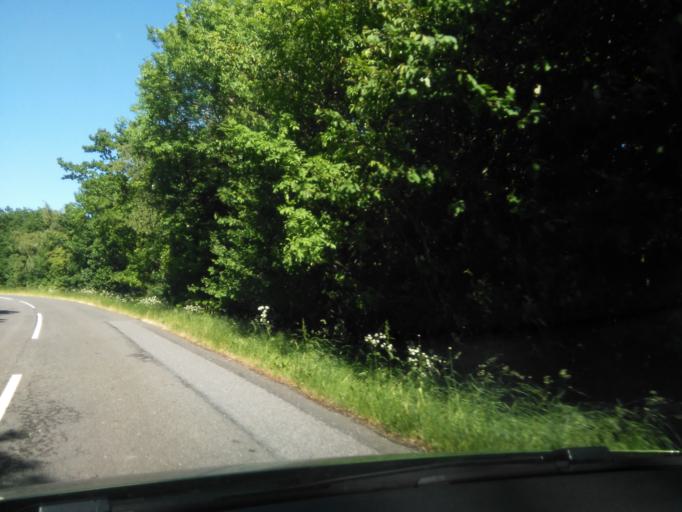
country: DK
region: Capital Region
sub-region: Bornholm Kommune
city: Nexo
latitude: 55.0657
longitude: 15.0819
